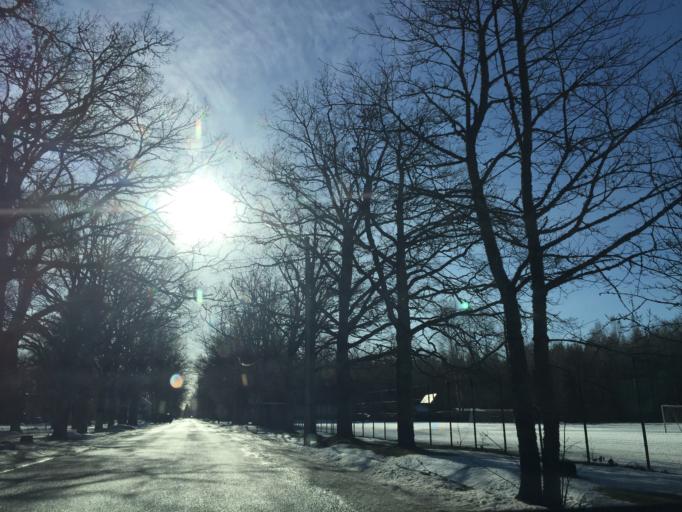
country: EE
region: Paernumaa
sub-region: Paikuse vald
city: Paikuse
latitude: 58.2814
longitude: 24.5756
